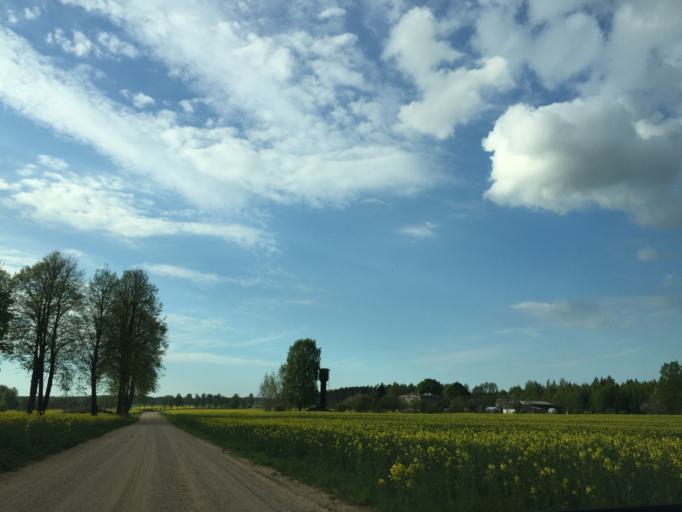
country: LV
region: Limbazu Rajons
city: Limbazi
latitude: 57.3507
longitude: 24.7027
